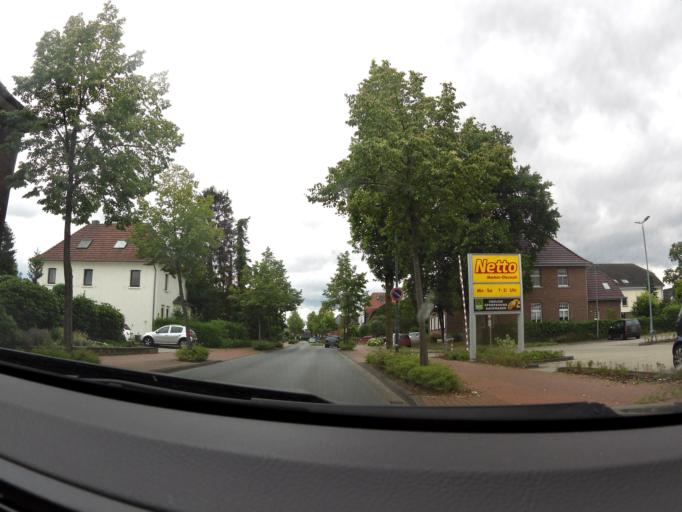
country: DE
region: North Rhine-Westphalia
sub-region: Regierungsbezirk Dusseldorf
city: Sonsbeck
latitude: 51.6060
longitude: 6.3766
